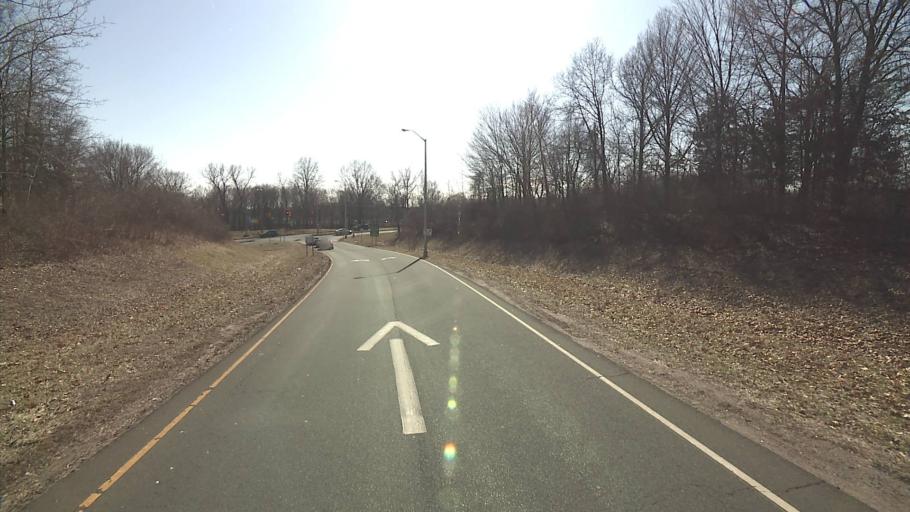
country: US
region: Connecticut
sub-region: Hartford County
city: Newington
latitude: 41.6997
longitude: -72.7587
